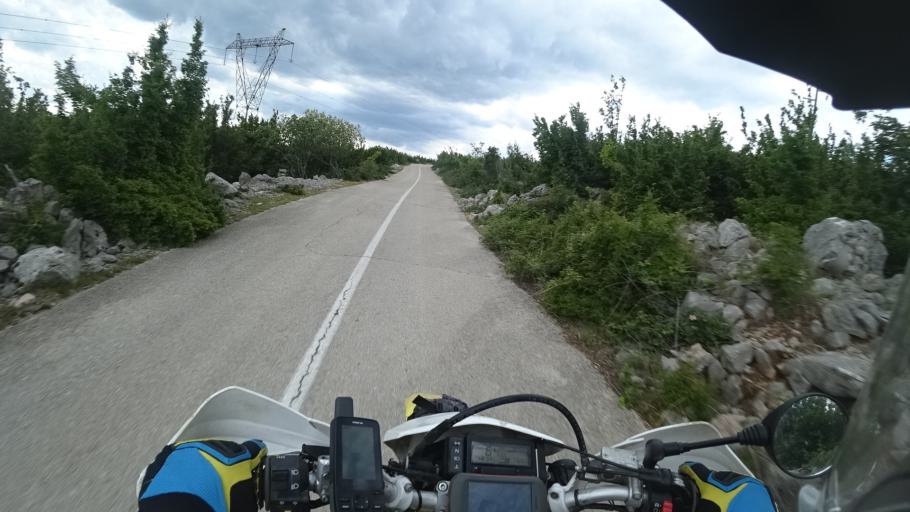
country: HR
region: Zadarska
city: Gracac
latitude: 44.2021
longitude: 15.8614
